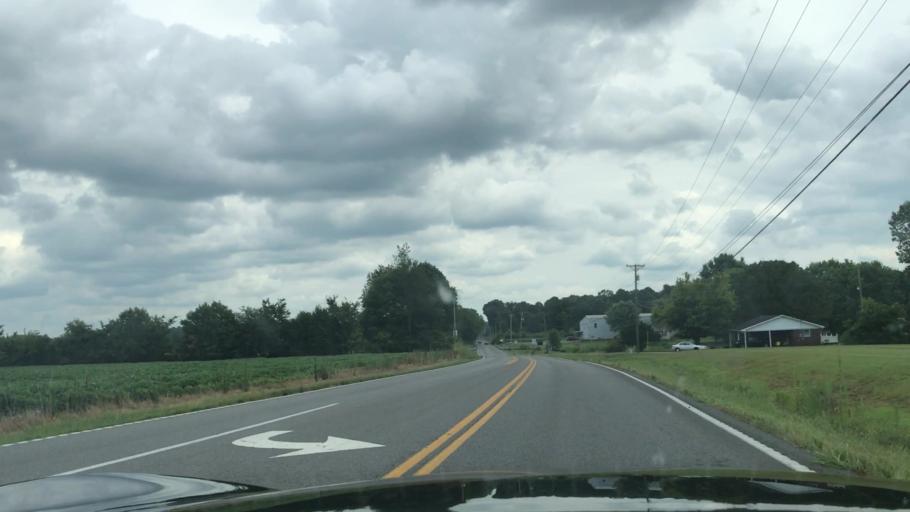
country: US
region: Kentucky
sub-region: Muhlenberg County
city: Greenville
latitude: 37.1975
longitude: -87.1273
